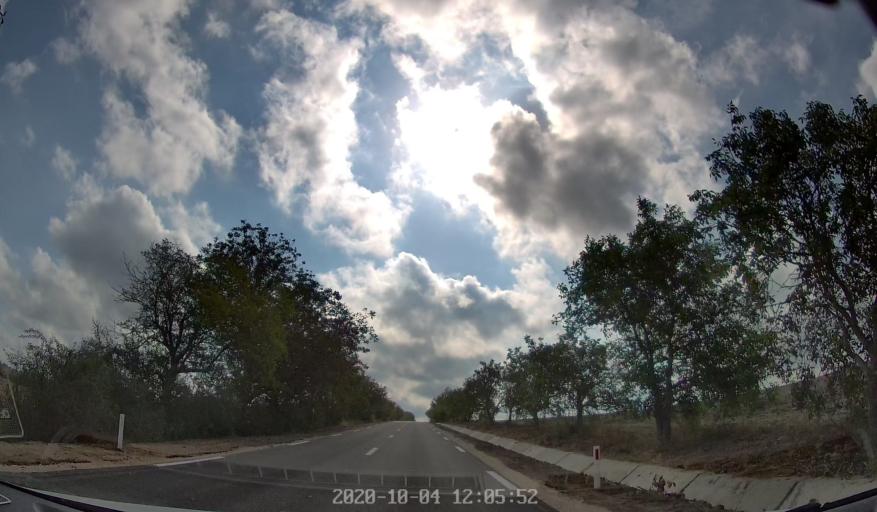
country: MD
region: Rezina
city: Saharna
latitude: 47.5895
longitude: 28.9534
